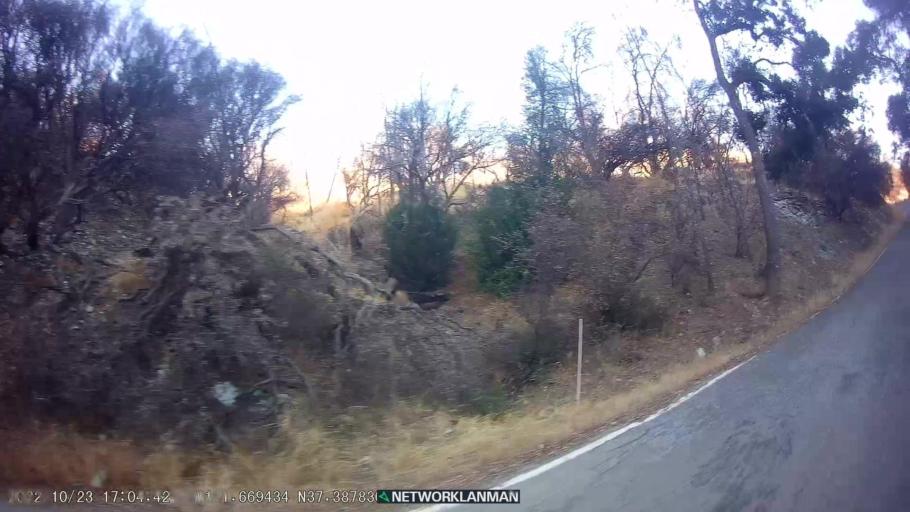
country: US
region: California
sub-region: Santa Clara County
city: East Foothills
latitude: 37.3879
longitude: -121.6693
